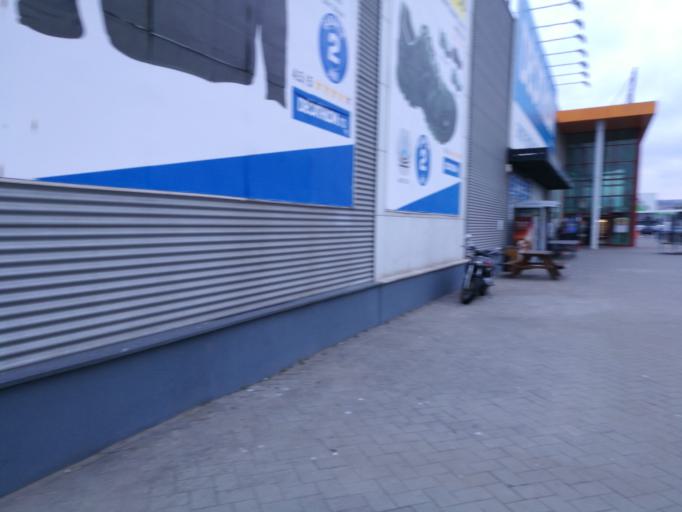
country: RO
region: Suceava
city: Suceava
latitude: 47.6636
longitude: 26.2663
